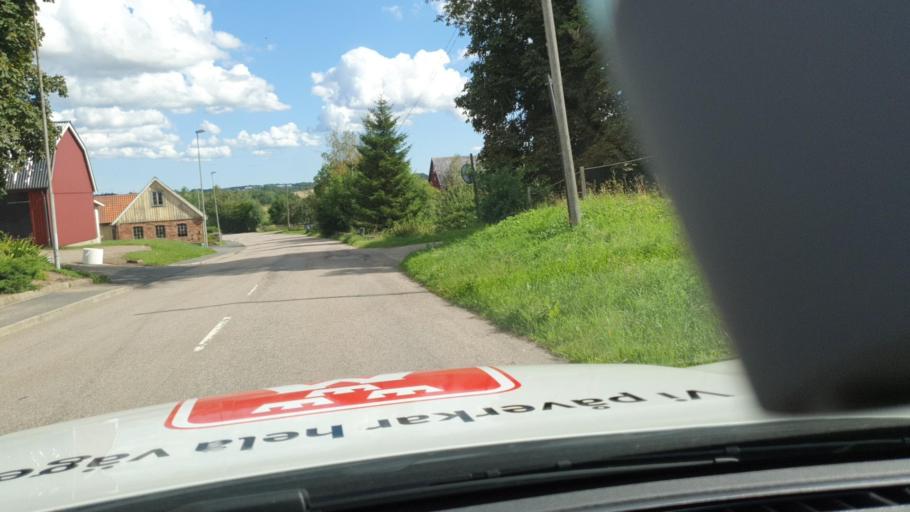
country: SE
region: Skane
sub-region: Astorps Kommun
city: Kvidinge
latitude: 56.1284
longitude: 13.0815
